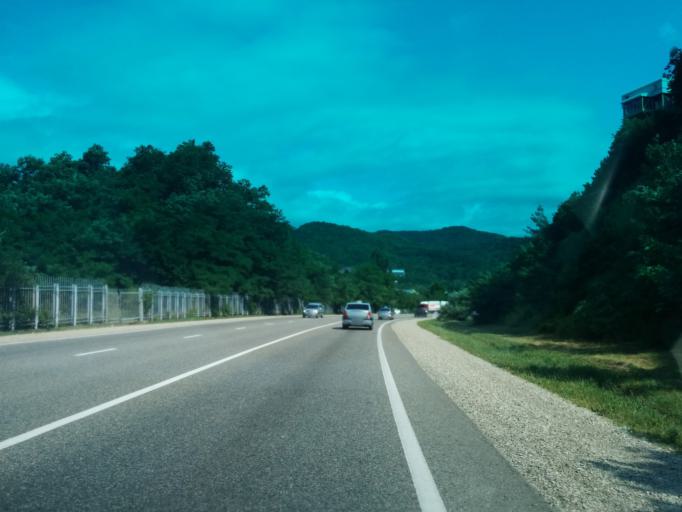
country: RU
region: Krasnodarskiy
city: Nebug
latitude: 44.1598
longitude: 39.0016
